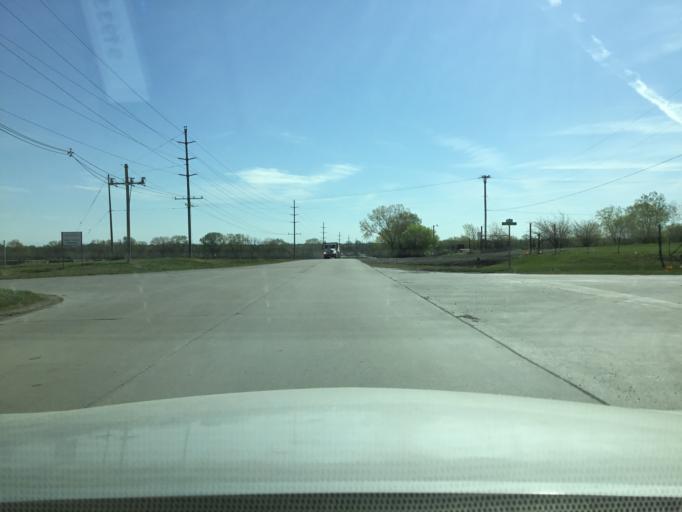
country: US
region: Kansas
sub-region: Neosho County
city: Chanute
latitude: 37.6963
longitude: -95.4583
